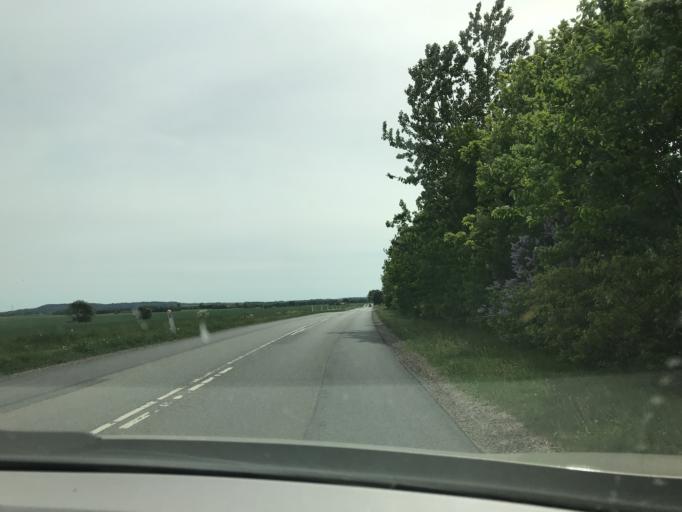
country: DK
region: Central Jutland
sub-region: Norddjurs Kommune
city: Allingabro
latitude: 56.4936
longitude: 10.3291
